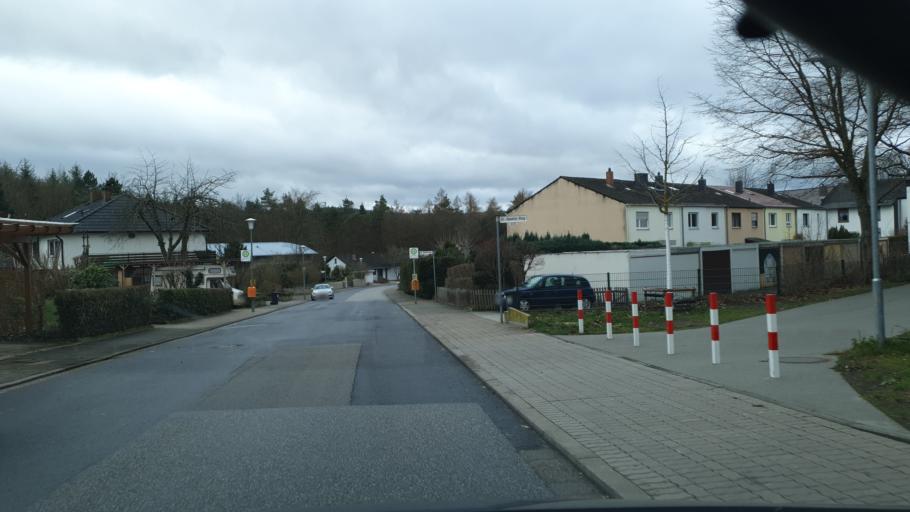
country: DE
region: Rheinland-Pfalz
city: Kaiserslautern
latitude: 49.4288
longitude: 7.7837
